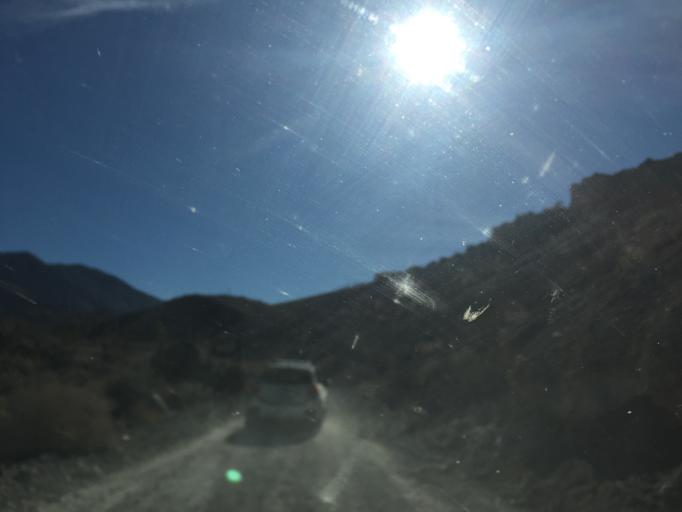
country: US
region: California
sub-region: Inyo County
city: Lone Pine
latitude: 36.8802
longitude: -117.5023
